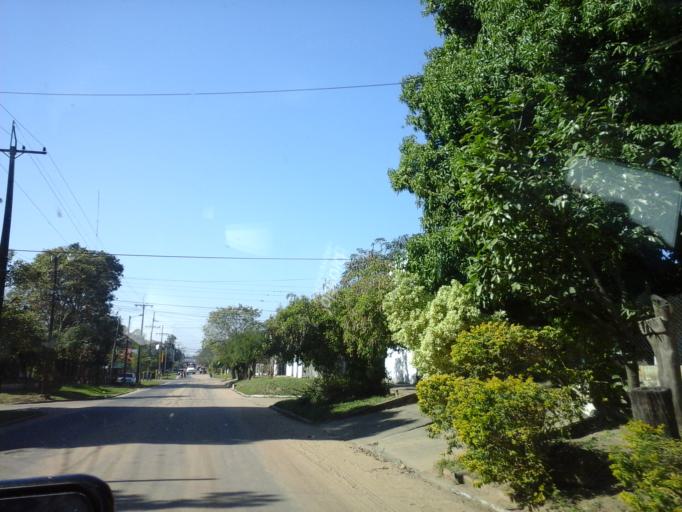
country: PY
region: Neembucu
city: Pilar
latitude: -26.8613
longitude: -58.3083
